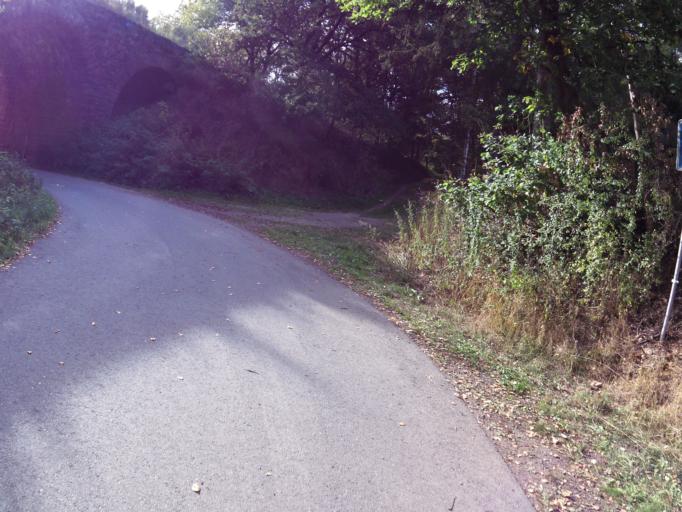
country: BE
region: Wallonia
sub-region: Province de Liege
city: Saint-Vith
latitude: 50.2463
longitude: 6.1501
